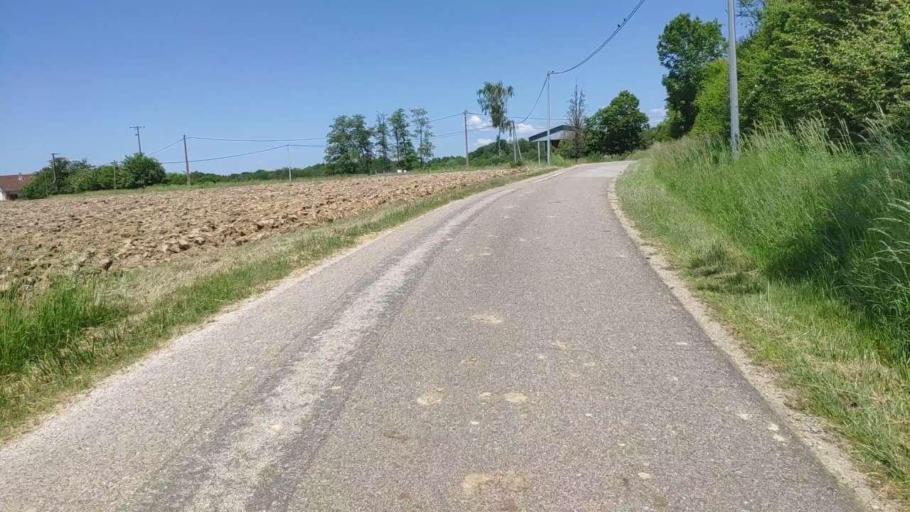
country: FR
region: Franche-Comte
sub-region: Departement du Jura
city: Bletterans
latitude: 46.7546
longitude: 5.4236
